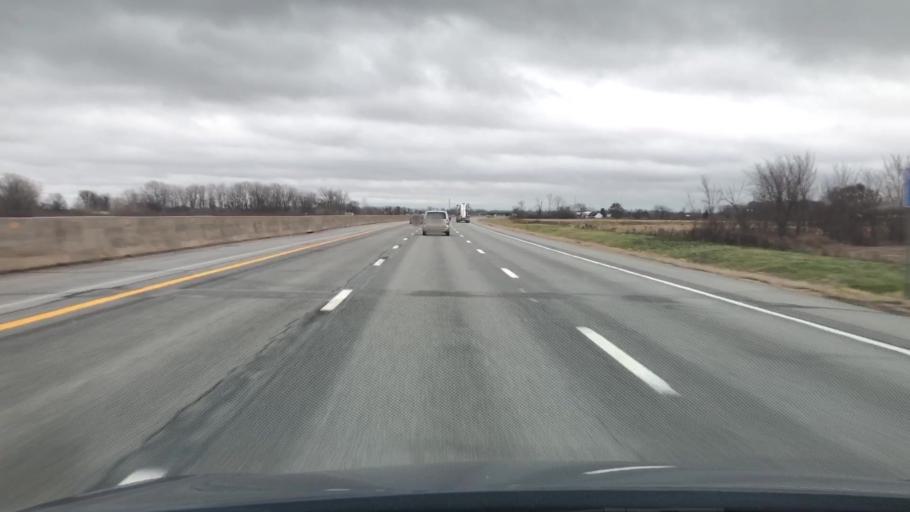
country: US
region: Ohio
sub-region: Sandusky County
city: Stony Prairie
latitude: 41.4198
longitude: -83.1638
